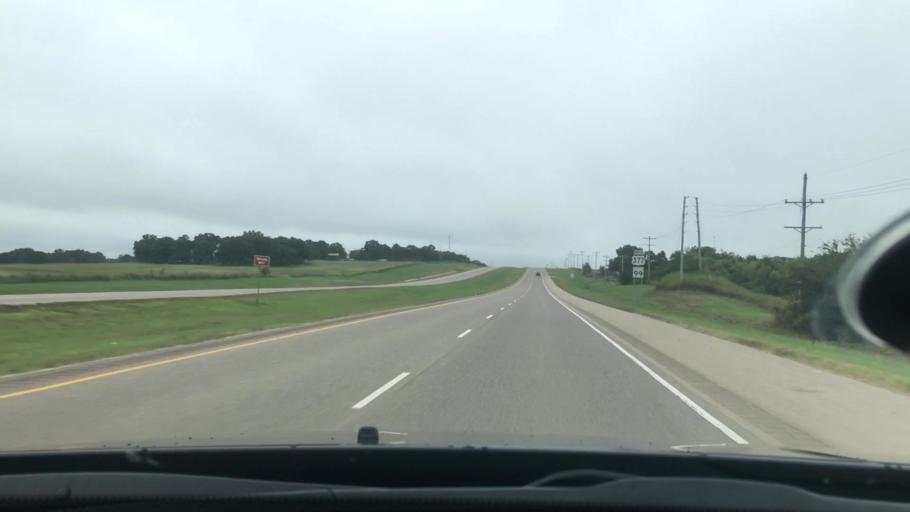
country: US
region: Oklahoma
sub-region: Lincoln County
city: Prague
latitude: 35.3628
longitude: -96.6715
